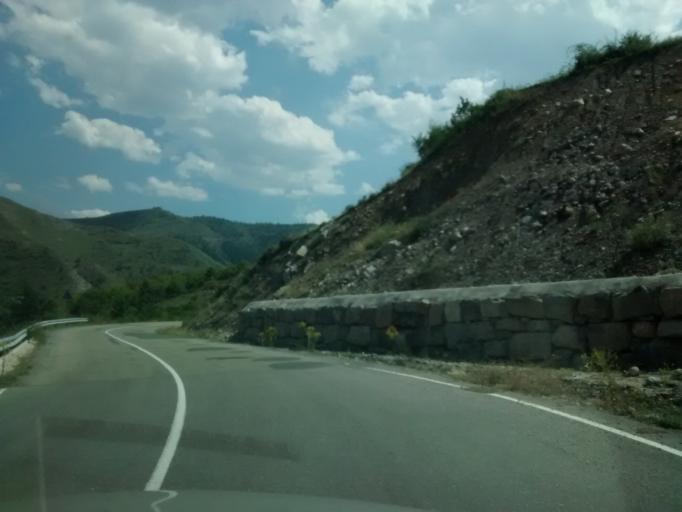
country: ES
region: La Rioja
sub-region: Provincia de La Rioja
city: Soto en Cameros
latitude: 42.2758
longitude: -2.4343
